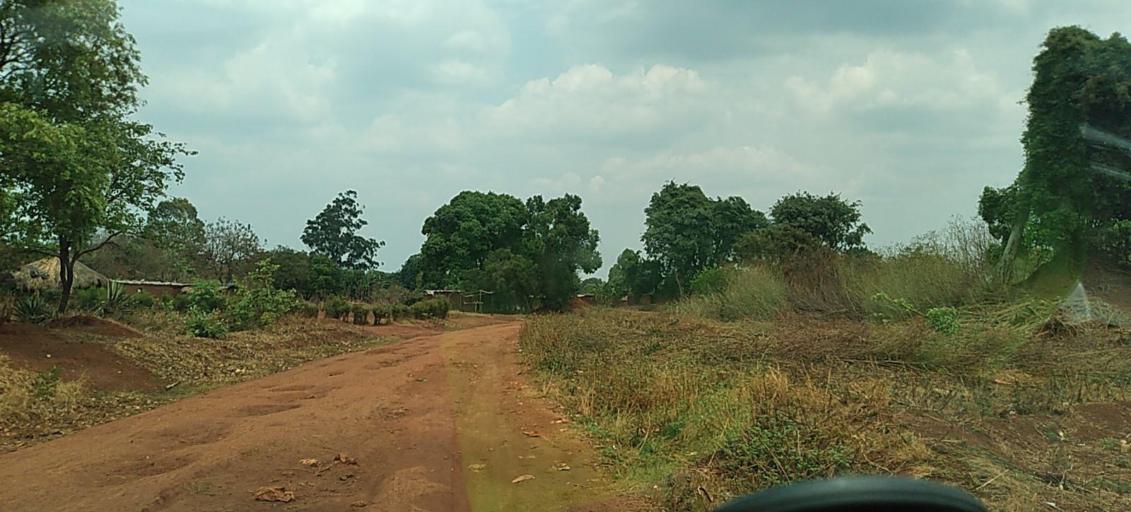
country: ZM
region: North-Western
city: Kansanshi
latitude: -12.0438
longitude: 26.3939
